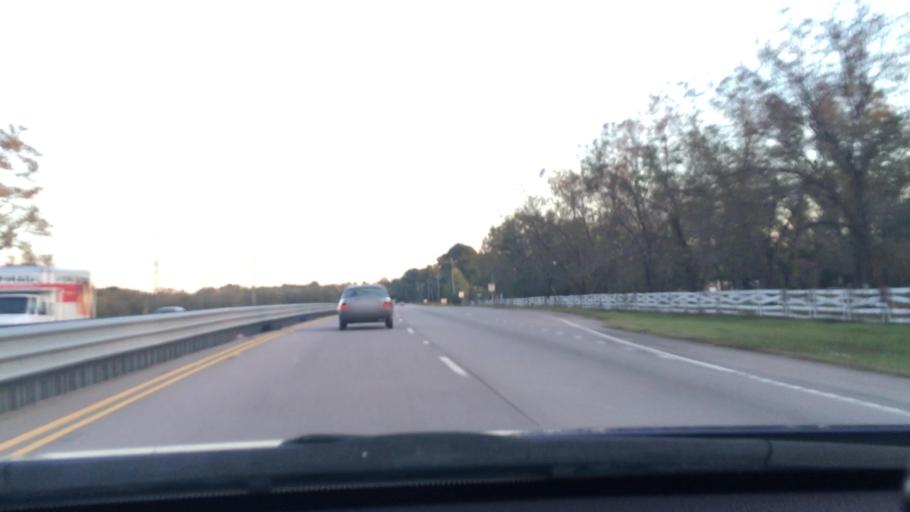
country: US
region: South Carolina
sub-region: Richland County
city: Hopkins
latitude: 33.9453
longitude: -80.8069
